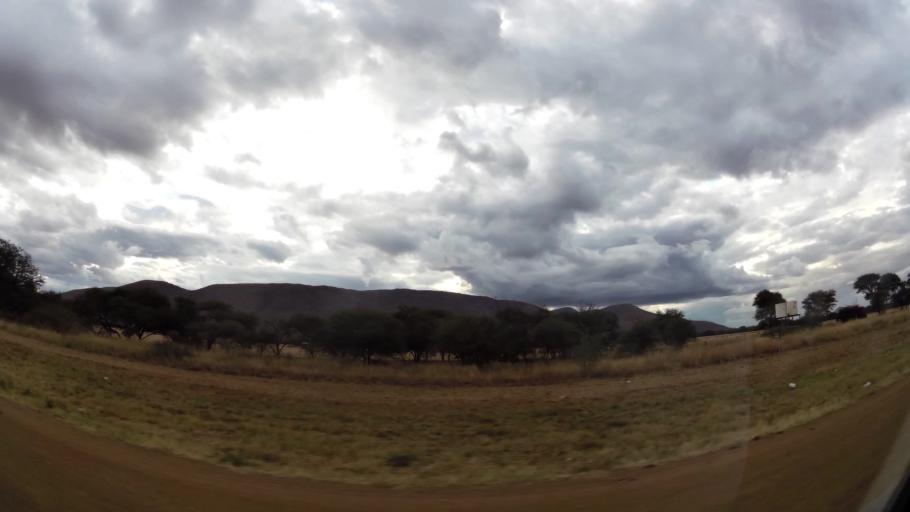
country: ZA
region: Limpopo
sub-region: Waterberg District Municipality
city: Mokopane
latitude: -24.2460
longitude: 28.9924
